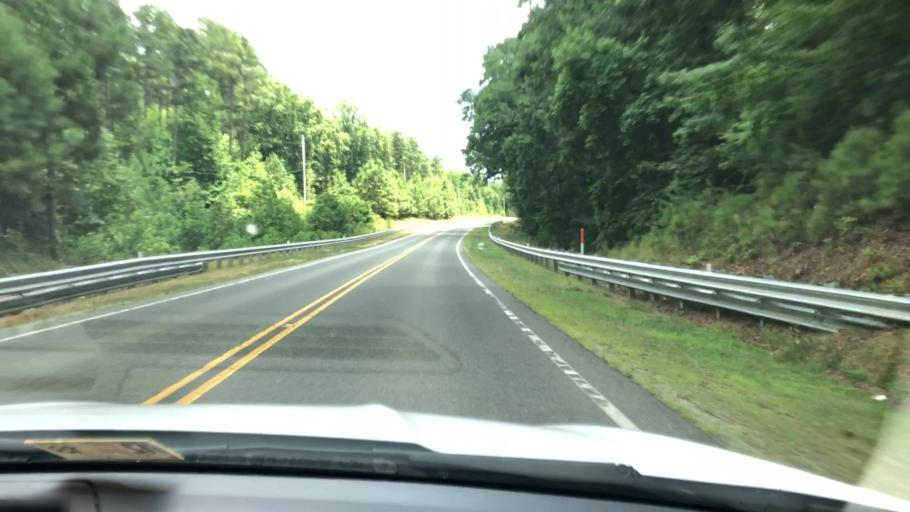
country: US
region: Virginia
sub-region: Lancaster County
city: Lancaster
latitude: 37.8263
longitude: -76.5628
